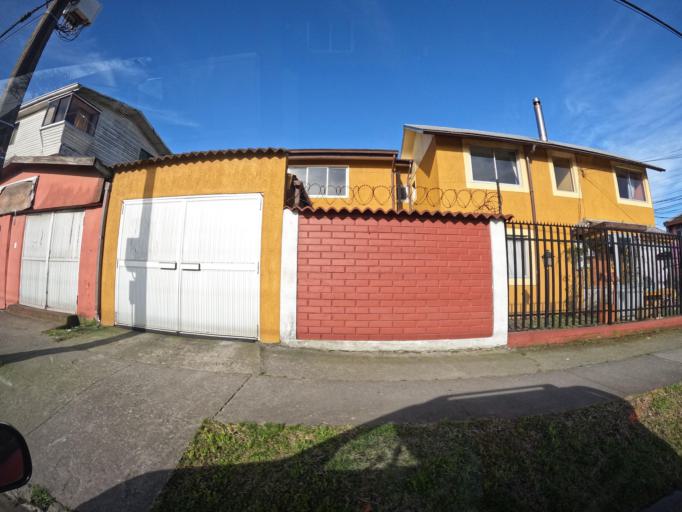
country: CL
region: Biobio
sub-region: Provincia de Concepcion
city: Talcahuano
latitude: -36.7496
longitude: -73.0873
